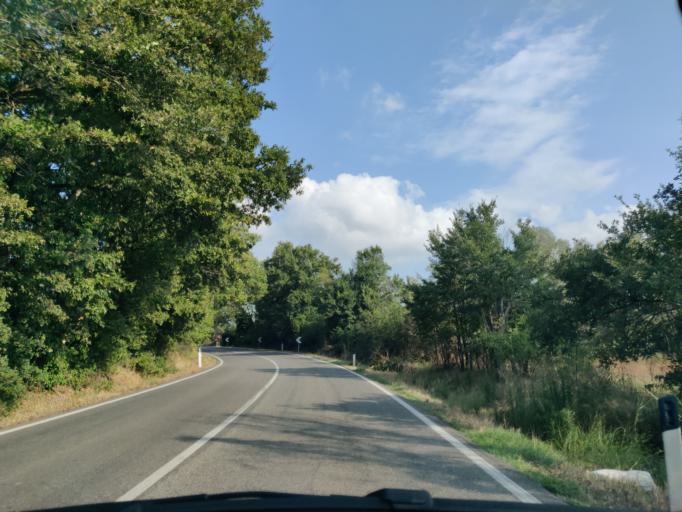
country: IT
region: Latium
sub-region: Provincia di Viterbo
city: Monte Romano
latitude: 42.2624
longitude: 11.8532
